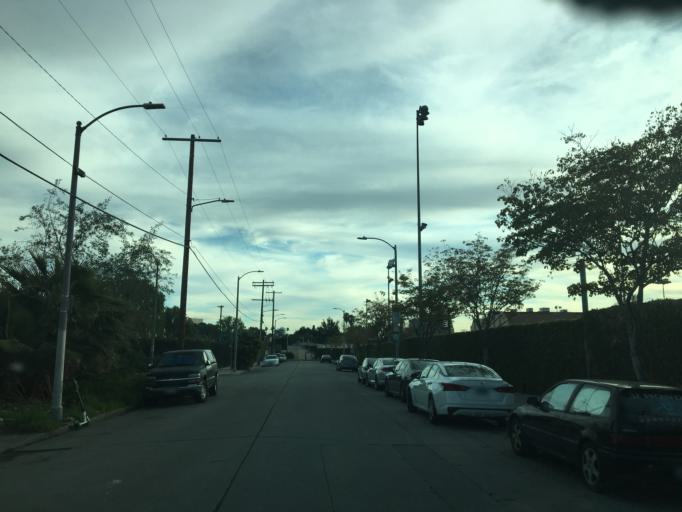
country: US
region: California
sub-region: Los Angeles County
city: Silver Lake
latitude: 34.0757
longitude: -118.2894
